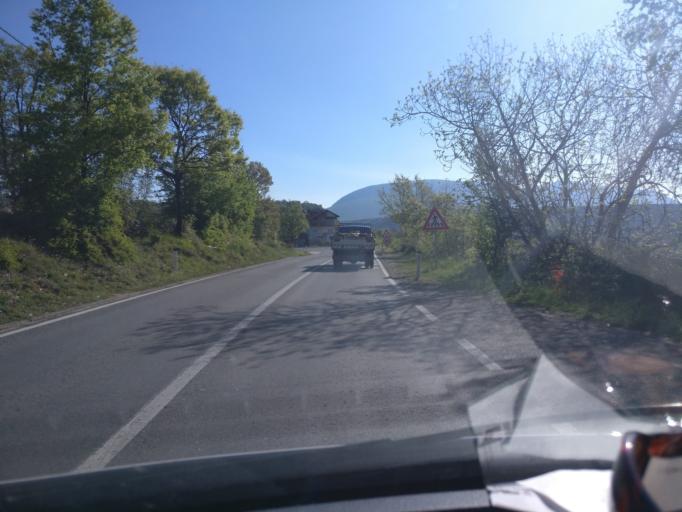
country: BA
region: Federation of Bosnia and Herzegovina
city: Crnici
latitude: 43.1037
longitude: 17.9056
